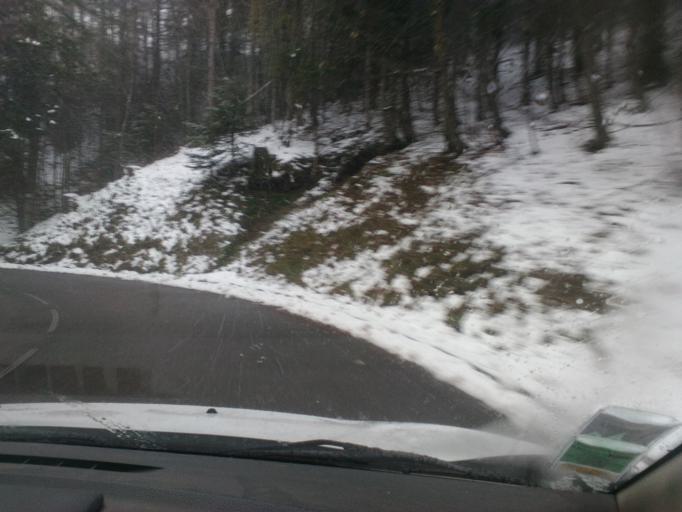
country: FR
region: Lorraine
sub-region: Departement des Vosges
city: Xonrupt-Longemer
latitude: 48.0637
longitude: 6.9953
